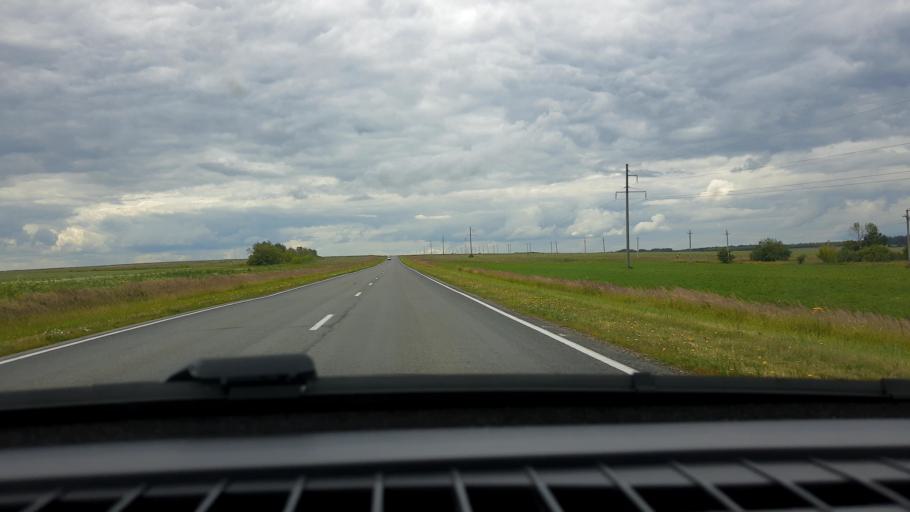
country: RU
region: Nizjnij Novgorod
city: Sergach
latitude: 55.5455
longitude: 45.5190
